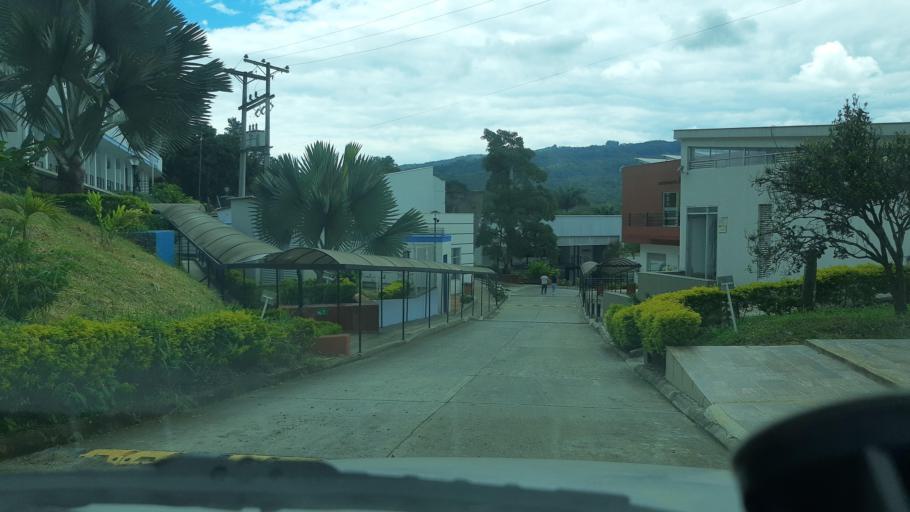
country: CO
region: Boyaca
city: Moniquira
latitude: 5.8811
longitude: -73.5786
